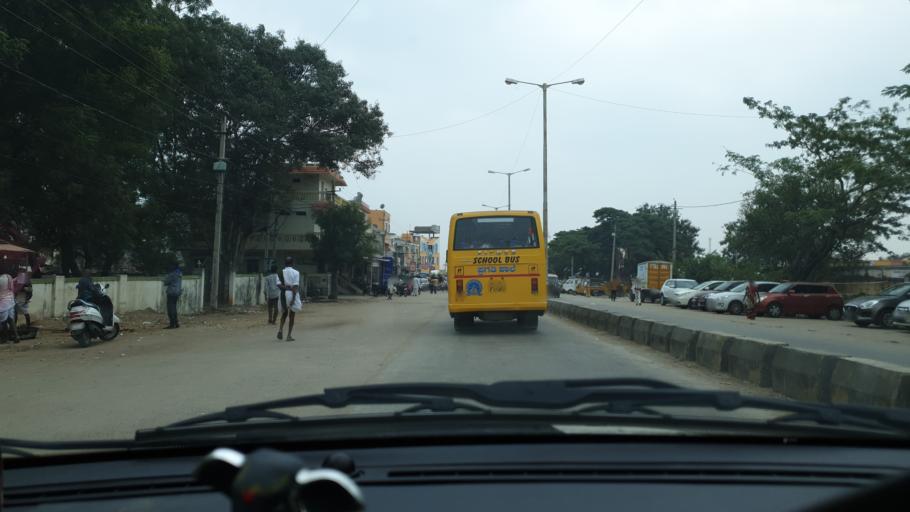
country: IN
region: Karnataka
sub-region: Yadgir
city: Gurmatkal
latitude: 16.8728
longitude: 77.3904
